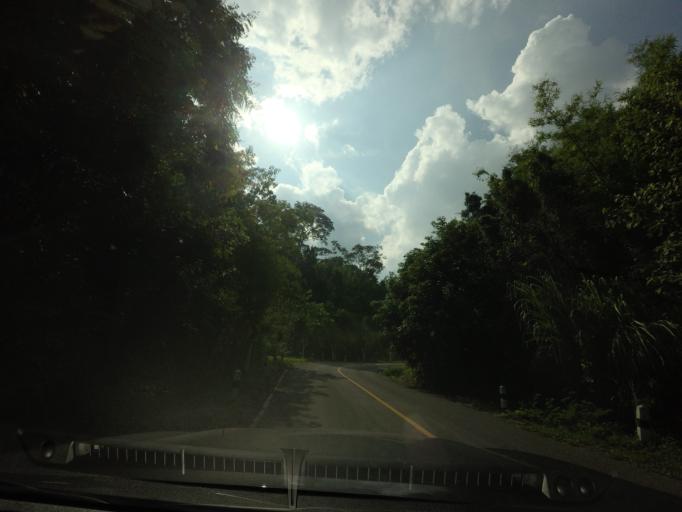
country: TH
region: Uttaradit
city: Ban Khok
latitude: 18.1983
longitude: 101.0529
